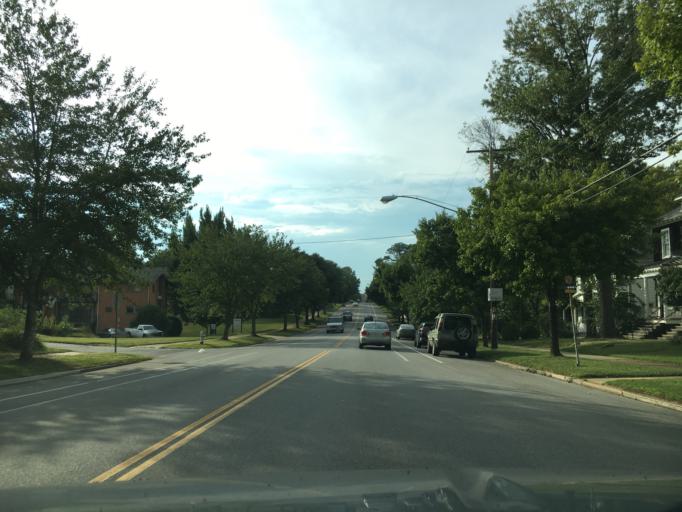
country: US
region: Virginia
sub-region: City of Lynchburg
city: Lynchburg
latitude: 37.4330
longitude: -79.1578
